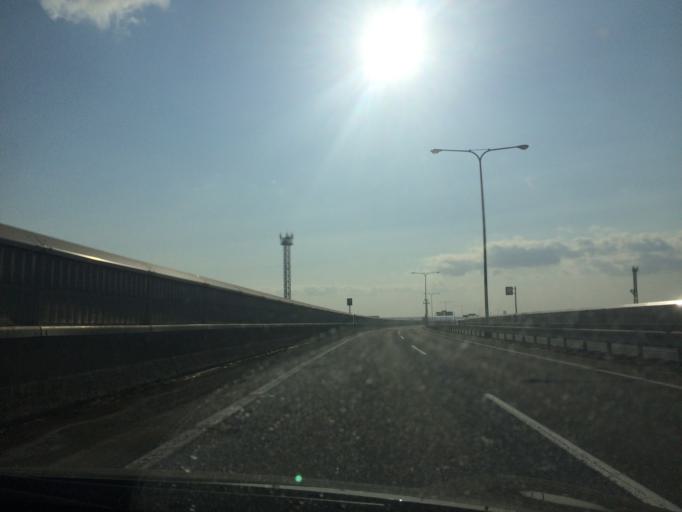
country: JP
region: Hokkaido
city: Sapporo
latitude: 43.0898
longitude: 141.4120
